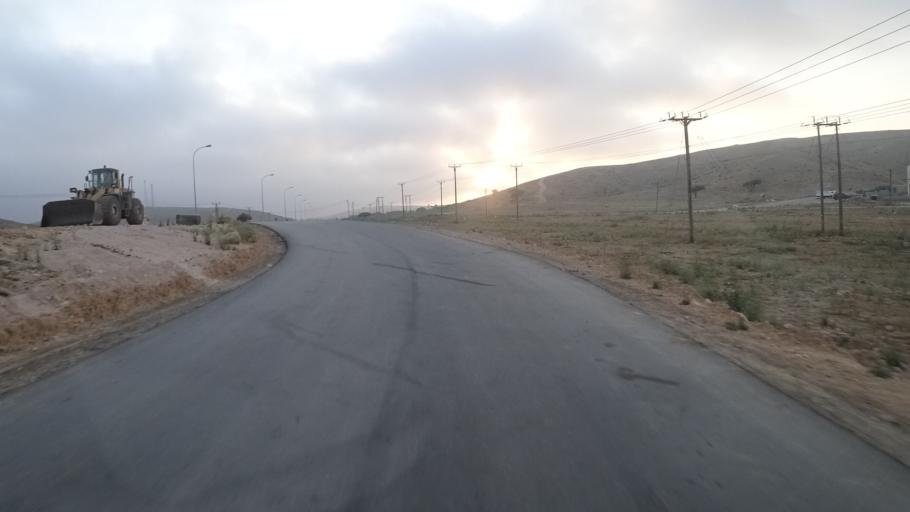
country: OM
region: Zufar
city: Salalah
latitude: 17.1264
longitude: 53.9440
